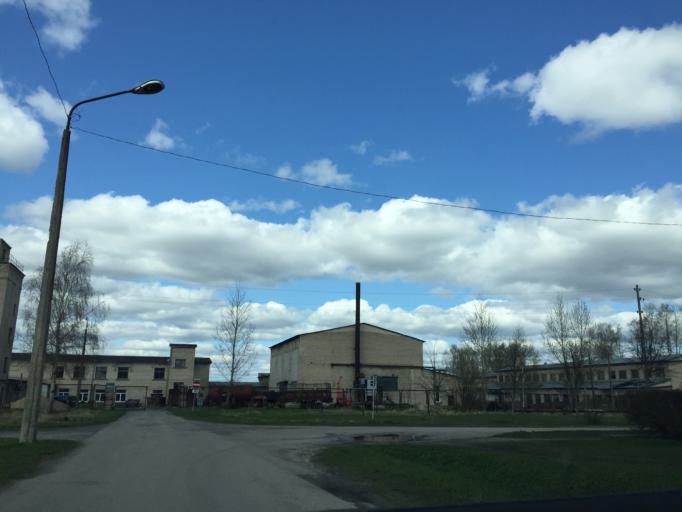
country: LV
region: Rezekne
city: Rezekne
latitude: 56.6964
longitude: 27.2318
